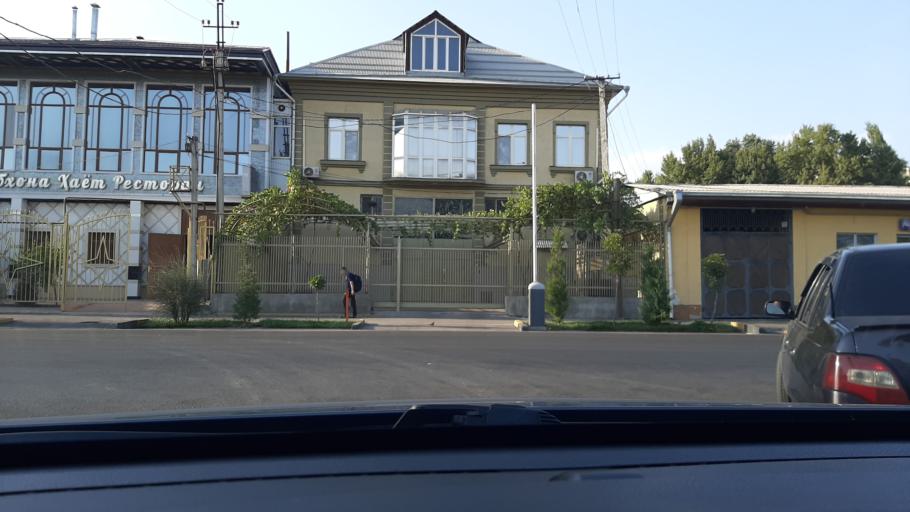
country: TJ
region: Dushanbe
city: Dushanbe
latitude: 38.5676
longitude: 68.8118
